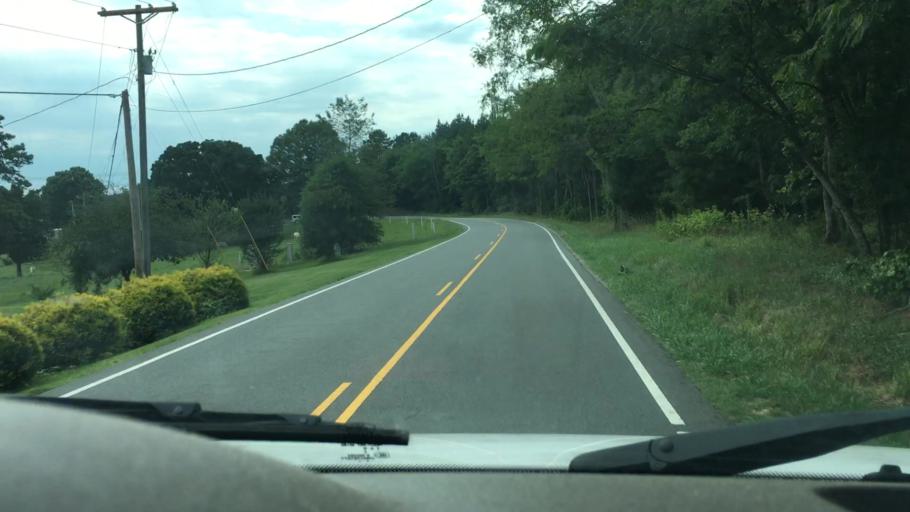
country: US
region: North Carolina
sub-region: Gaston County
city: Davidson
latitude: 35.4828
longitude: -80.8095
